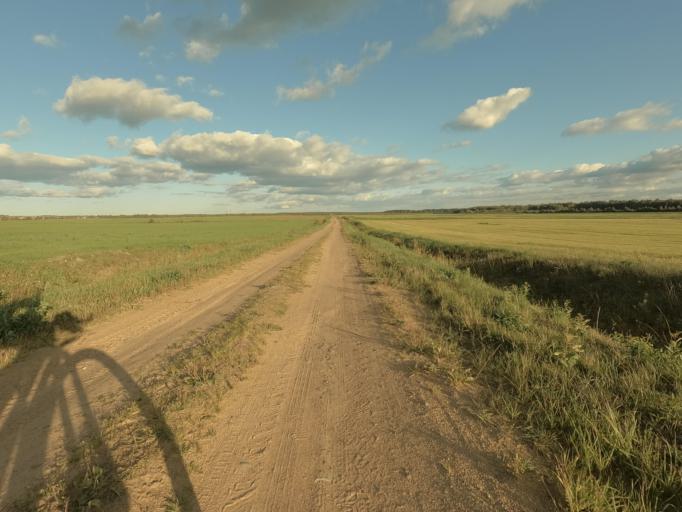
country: RU
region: Leningrad
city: Imeni Sverdlova
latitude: 59.8637
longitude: 30.7418
